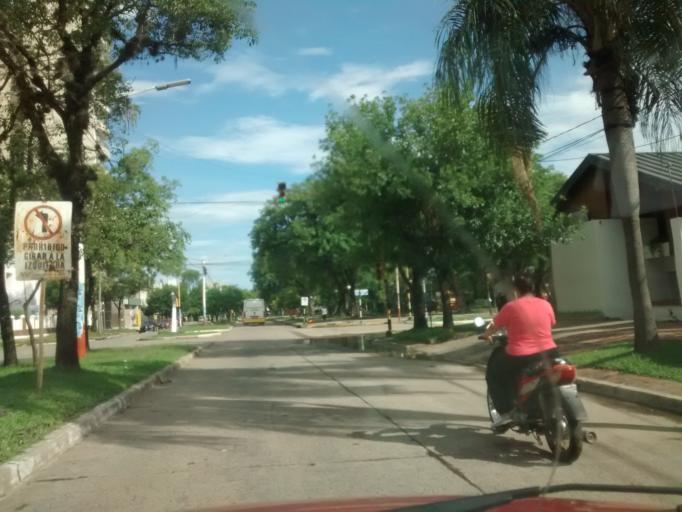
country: AR
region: Chaco
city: Resistencia
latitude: -27.4431
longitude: -58.9868
